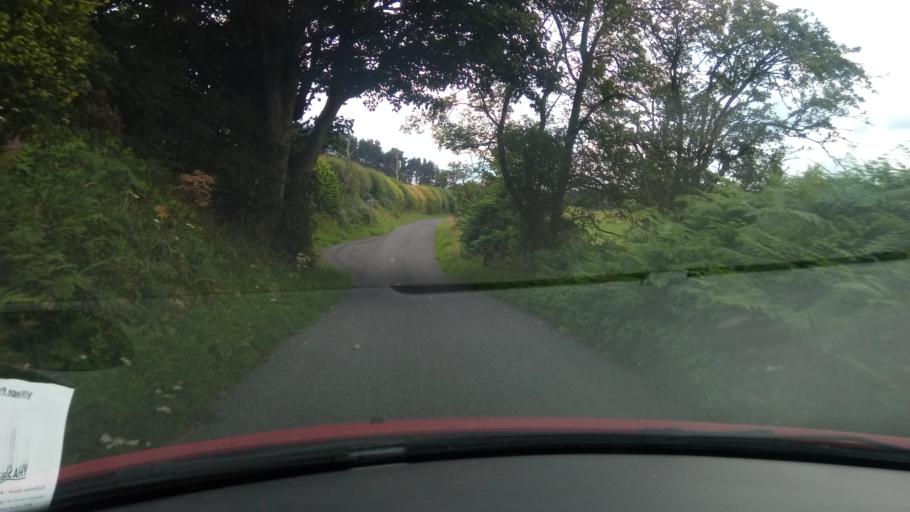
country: GB
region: Scotland
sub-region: The Scottish Borders
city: Jedburgh
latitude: 55.4062
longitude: -2.6465
